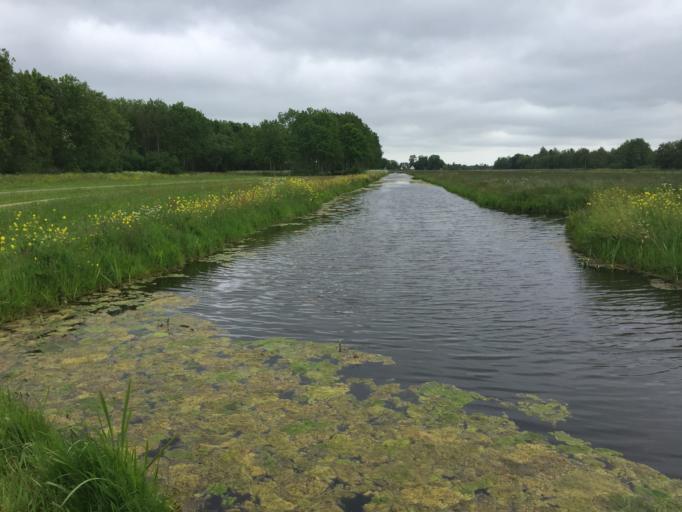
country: NL
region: South Holland
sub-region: Bodegraven-Reeuwijk
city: Reeuwijk
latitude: 52.0172
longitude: 4.7441
